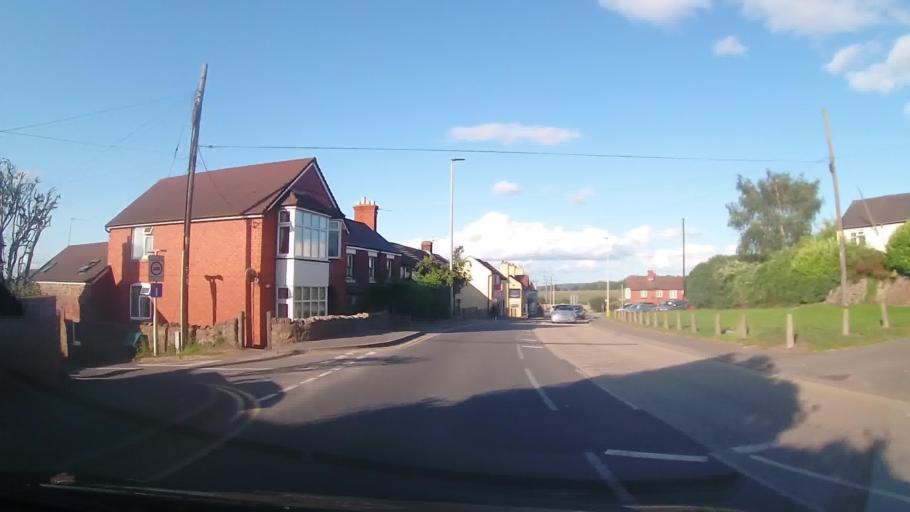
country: GB
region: England
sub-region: Shropshire
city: Bayston Hill
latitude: 52.6756
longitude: -2.7605
